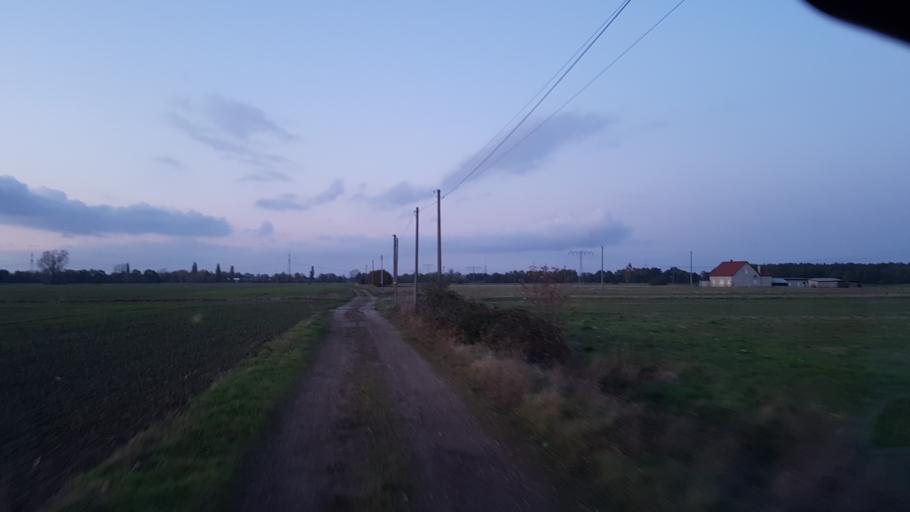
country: DE
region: Brandenburg
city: Doberlug-Kirchhain
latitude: 51.6354
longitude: 13.5842
